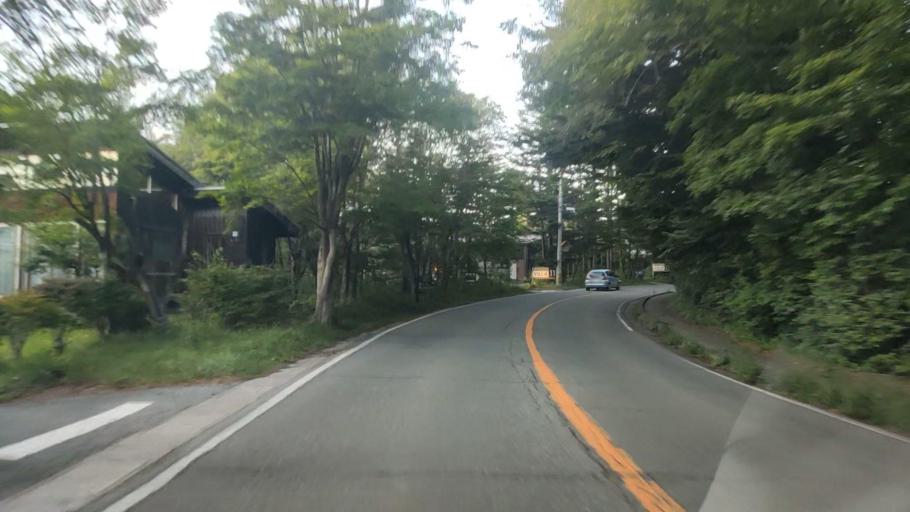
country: JP
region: Nagano
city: Komoro
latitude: 36.3673
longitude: 138.5872
